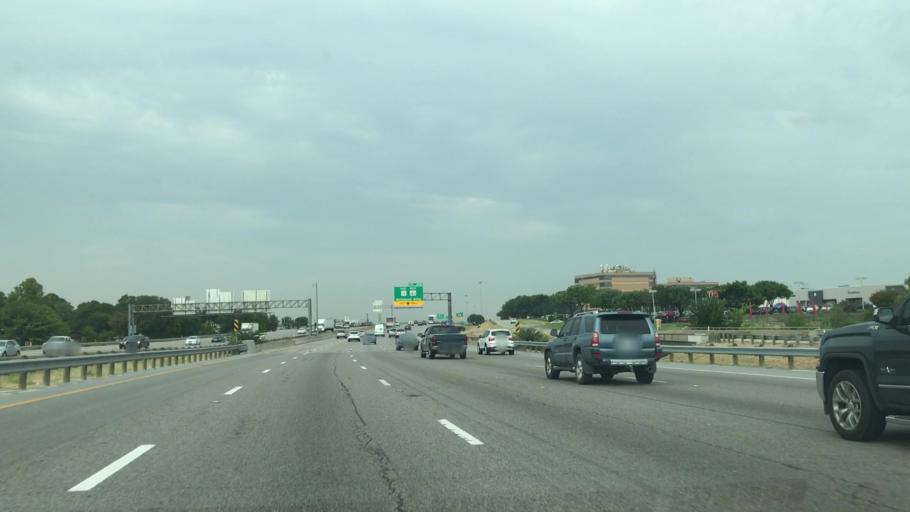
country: US
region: Texas
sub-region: Tarrant County
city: Richland Hills
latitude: 32.8176
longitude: -97.2062
